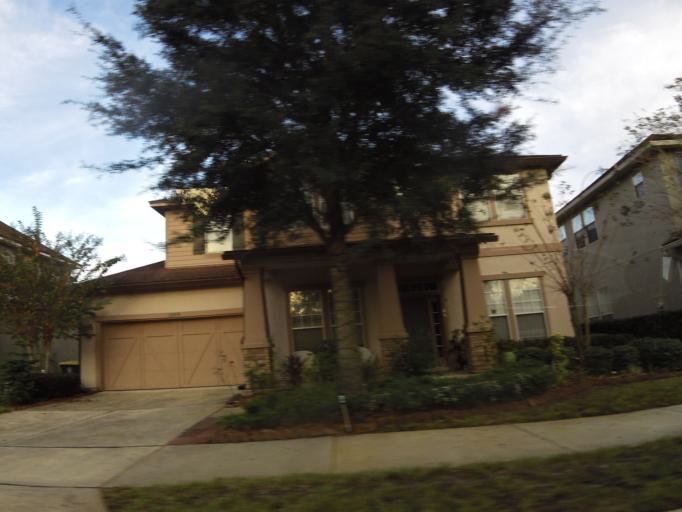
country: US
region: Florida
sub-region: Saint Johns County
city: Fruit Cove
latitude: 30.1548
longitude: -81.5472
